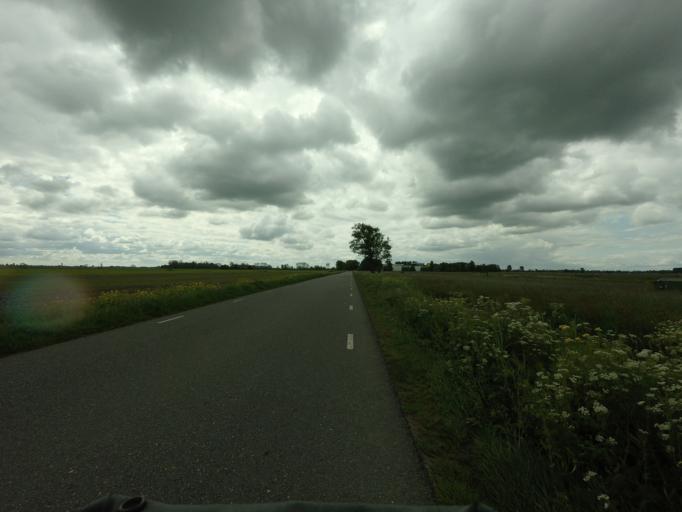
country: NL
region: Utrecht
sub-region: Gemeente Lopik
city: Lopik
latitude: 51.9398
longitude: 4.9353
